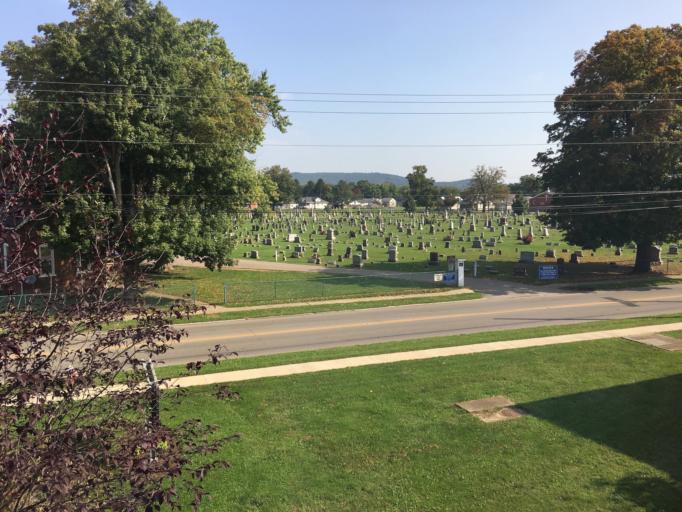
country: US
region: Ohio
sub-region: Ross County
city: Chillicothe
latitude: 39.3248
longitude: -82.9625
